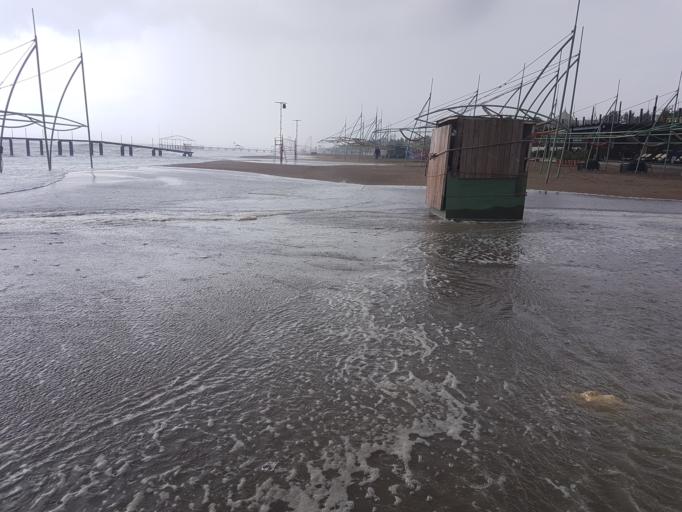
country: TR
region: Antalya
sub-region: Serik
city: Kumkoey
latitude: 36.8532
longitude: 30.8821
